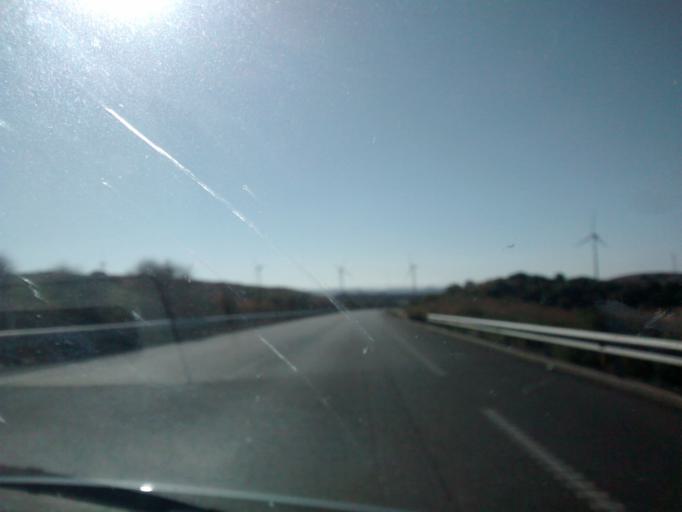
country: ES
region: Andalusia
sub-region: Provincia de Cadiz
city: Paterna de Rivera
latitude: 36.4778
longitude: -5.8834
